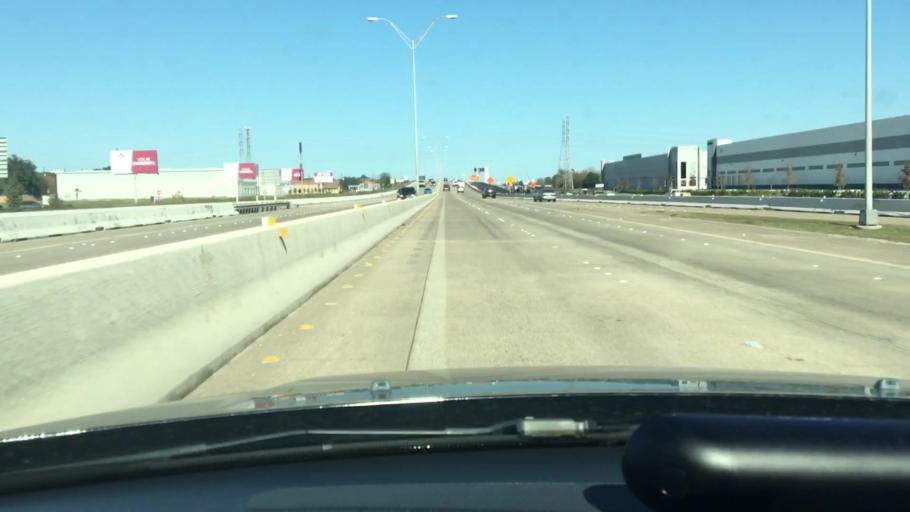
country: US
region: Texas
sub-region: Harris County
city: Deer Park
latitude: 29.6965
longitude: -95.1535
